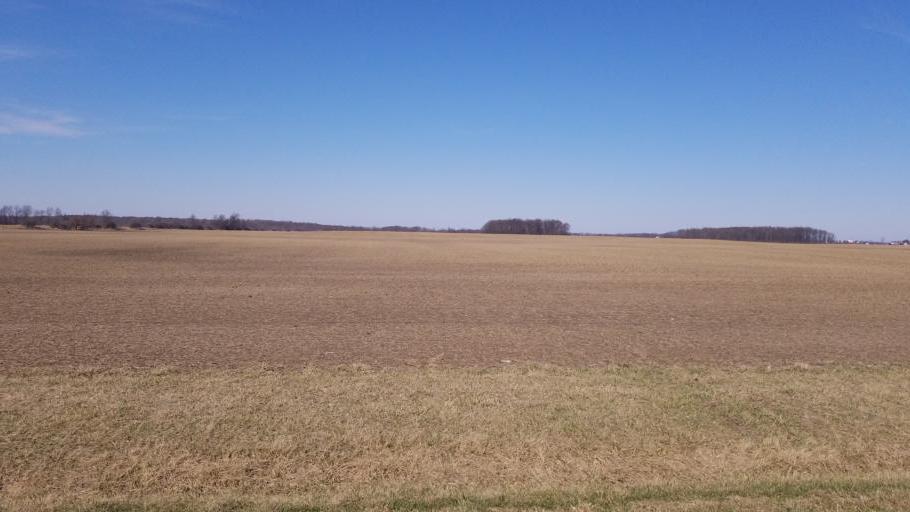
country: US
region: Ohio
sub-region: Hardin County
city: Kenton
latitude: 40.5415
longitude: -83.4541
